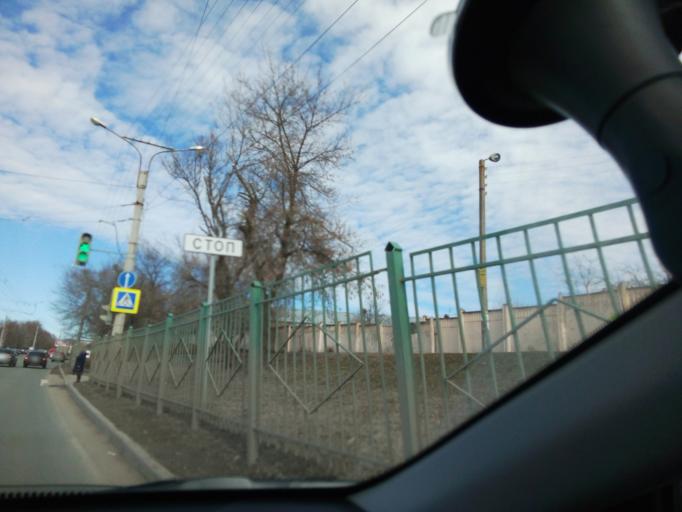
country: RU
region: Chuvashia
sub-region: Cheboksarskiy Rayon
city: Cheboksary
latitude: 56.1125
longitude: 47.2481
